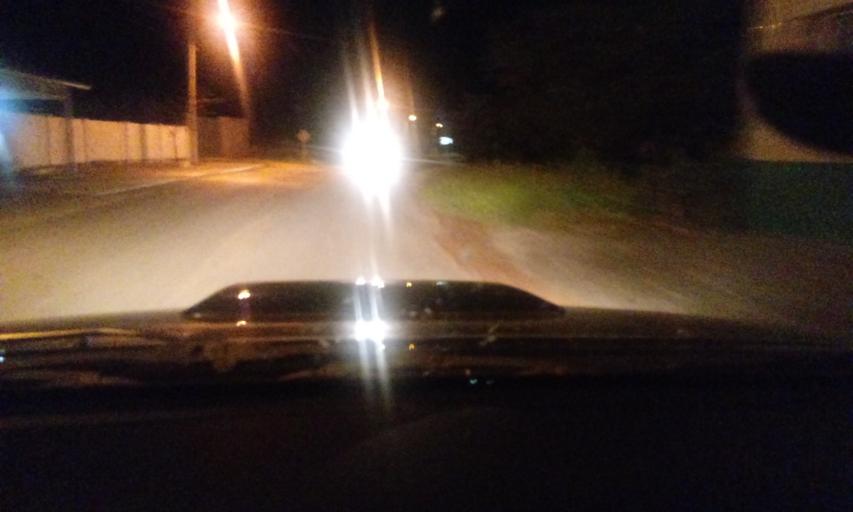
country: BR
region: Bahia
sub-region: Guanambi
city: Guanambi
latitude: -14.1978
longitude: -42.7954
